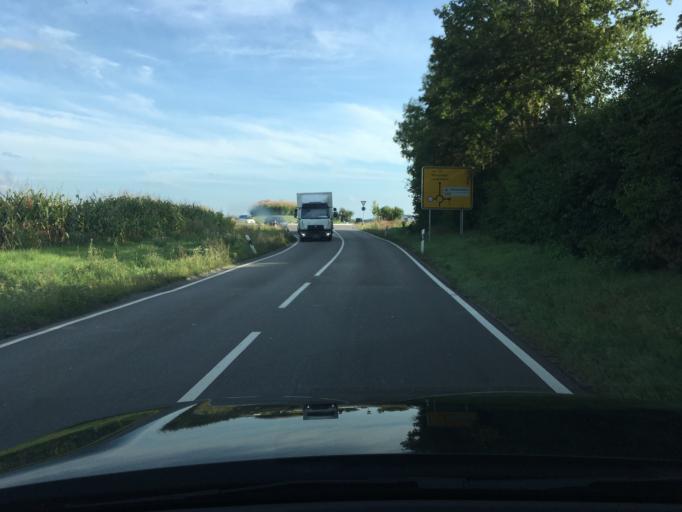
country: DE
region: Baden-Wuerttemberg
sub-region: Regierungsbezirk Stuttgart
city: Affalterbach
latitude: 48.9174
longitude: 9.3324
